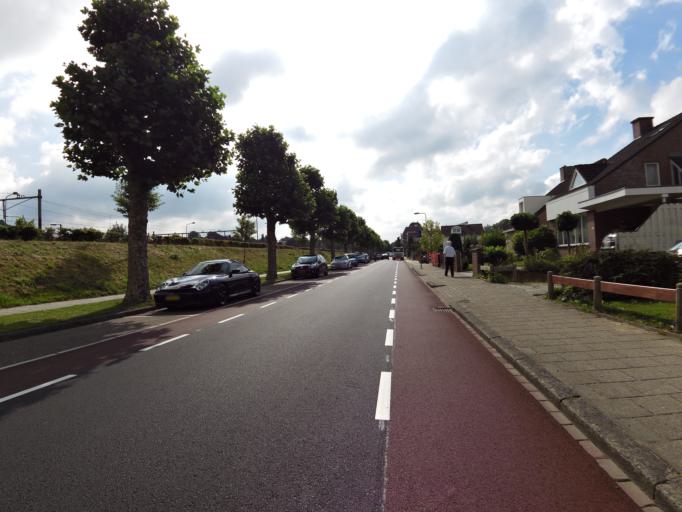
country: NL
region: Limburg
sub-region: Valkenburg aan de Geul
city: Valkenburg
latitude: 50.8703
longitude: 5.8295
